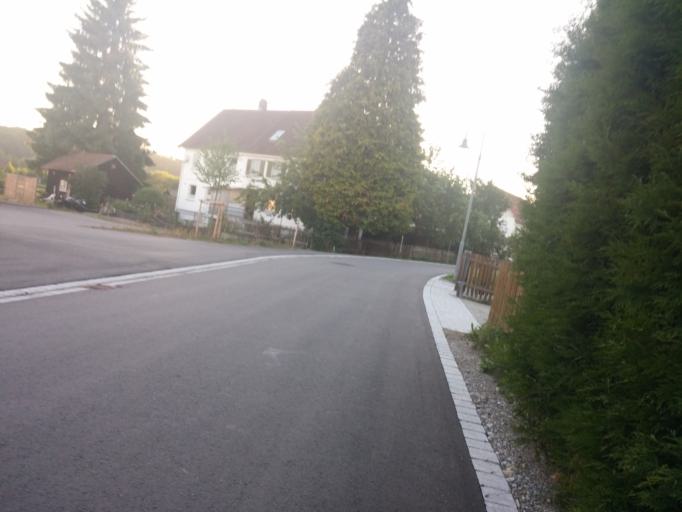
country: DE
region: Bavaria
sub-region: Swabia
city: Lautrach
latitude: 47.9018
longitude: 10.1249
